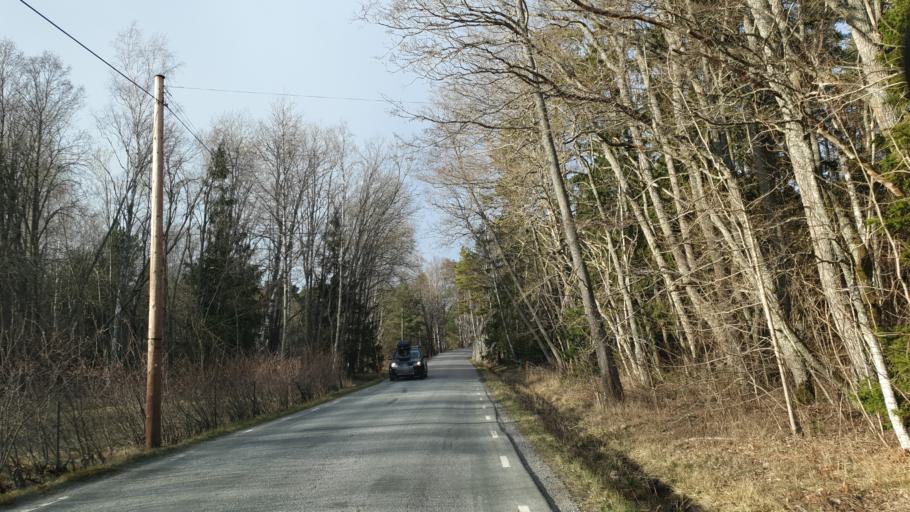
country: SE
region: Stockholm
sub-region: Varmdo Kommun
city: Holo
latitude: 59.3624
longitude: 18.6705
